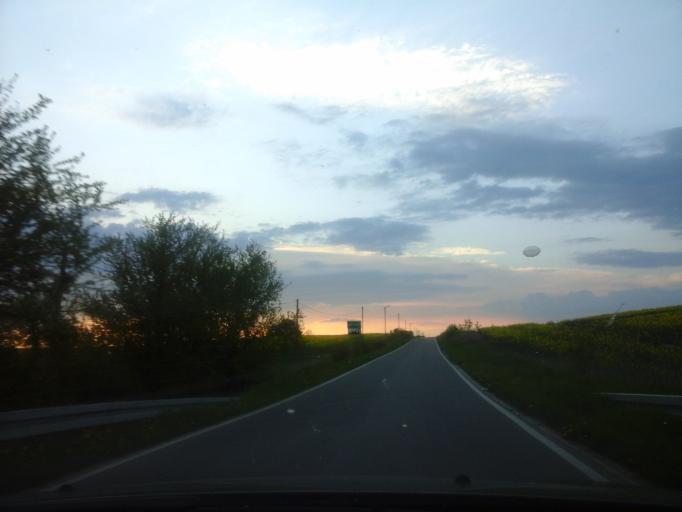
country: PL
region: West Pomeranian Voivodeship
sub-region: Powiat choszczenski
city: Pelczyce
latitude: 53.0356
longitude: 15.3262
